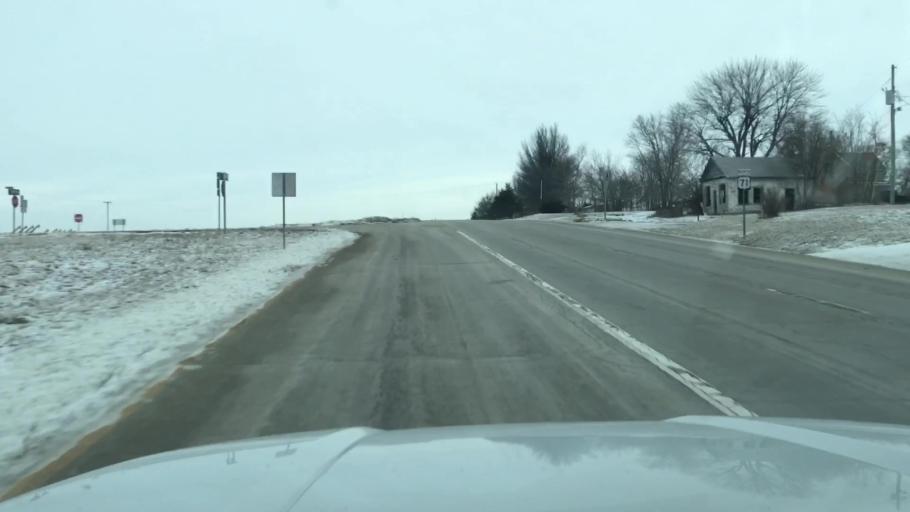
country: US
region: Missouri
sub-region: Andrew County
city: Savannah
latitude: 40.0247
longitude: -94.8794
